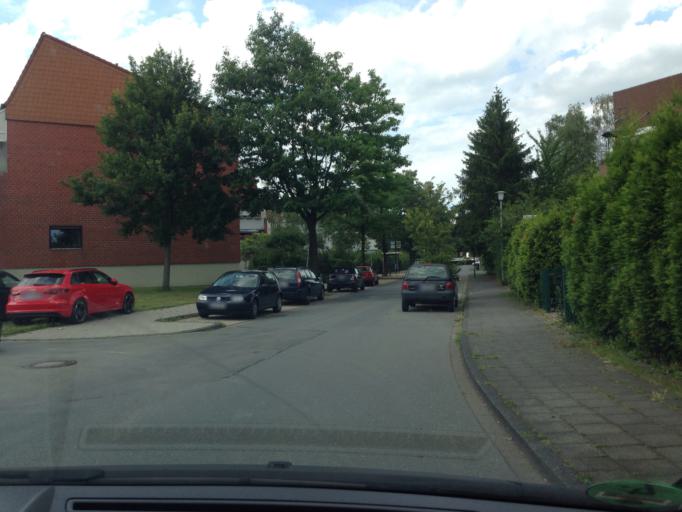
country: DE
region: North Rhine-Westphalia
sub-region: Regierungsbezirk Munster
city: Muenster
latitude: 51.9945
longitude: 7.5481
